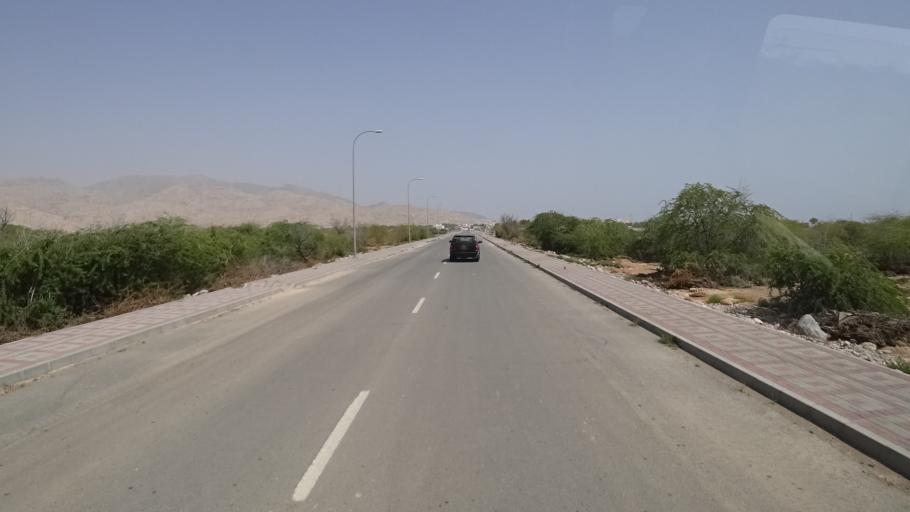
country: OM
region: Muhafazat Masqat
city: Muscat
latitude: 23.2462
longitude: 58.9117
